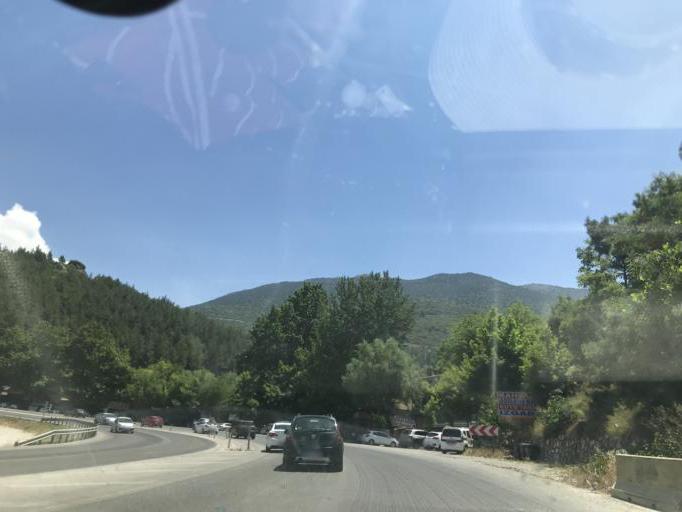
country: TR
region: Denizli
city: Denizli
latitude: 37.7283
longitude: 29.1660
